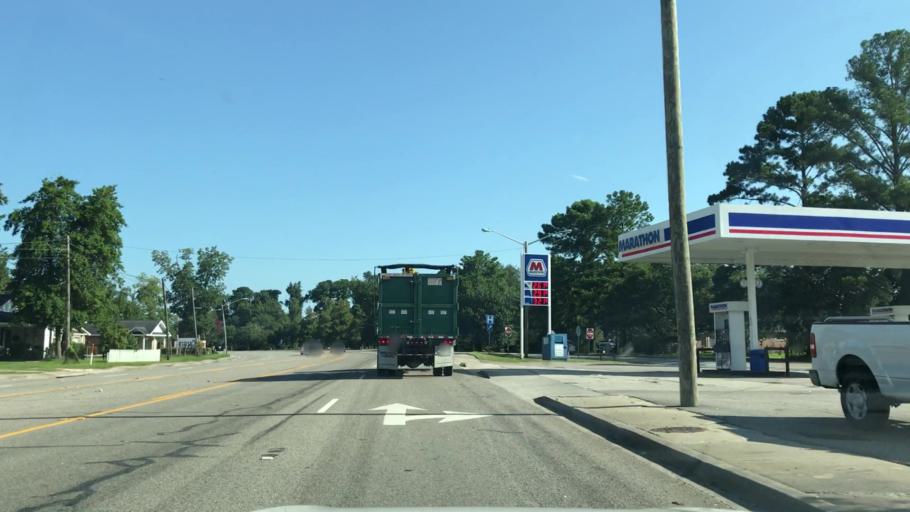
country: US
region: South Carolina
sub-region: Georgetown County
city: Georgetown
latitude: 33.3825
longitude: -79.2874
